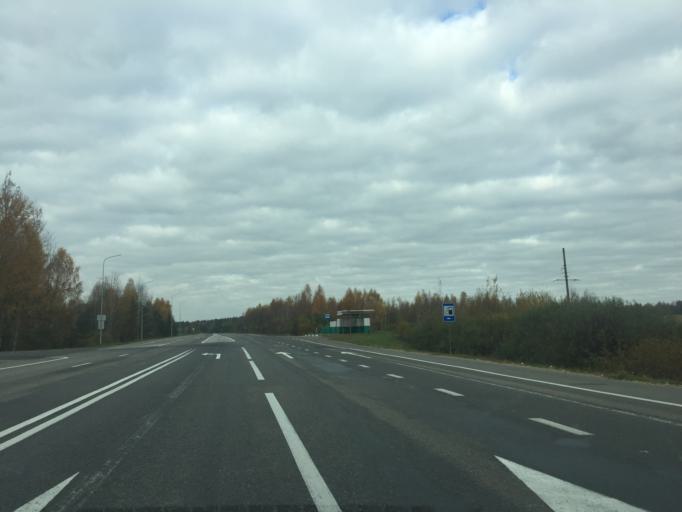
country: BY
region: Grodnenskaya
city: Baruny
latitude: 54.3918
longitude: 26.1226
